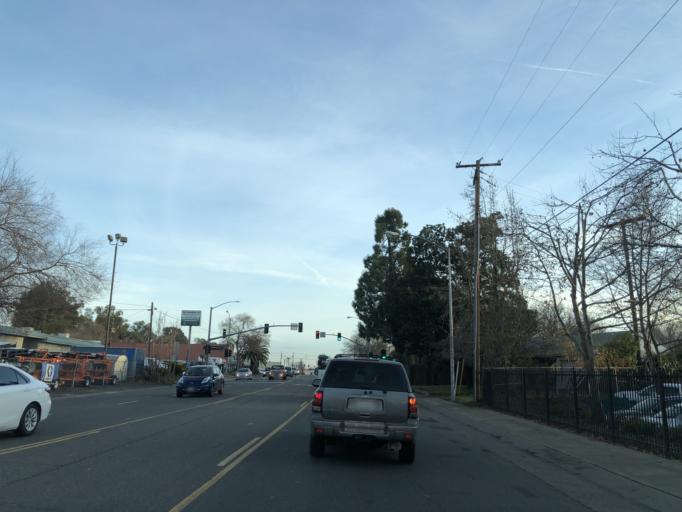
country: US
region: California
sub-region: Sacramento County
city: Rosemont
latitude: 38.5590
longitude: -121.4291
